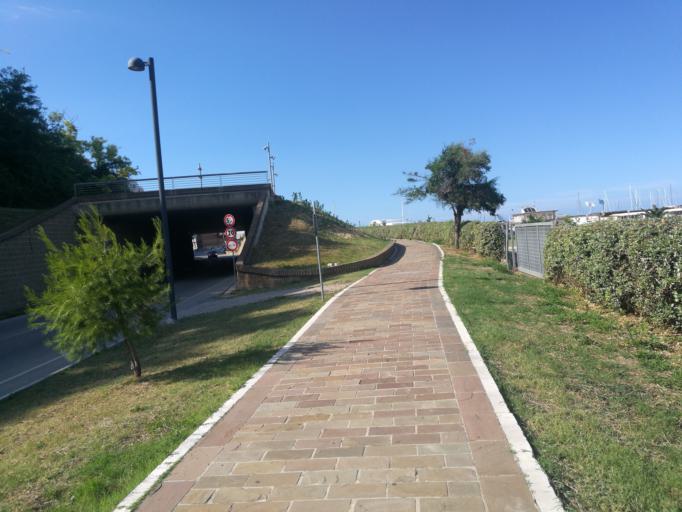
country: IT
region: Molise
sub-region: Provincia di Campobasso
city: Termoli
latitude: 42.0002
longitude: 14.9991
